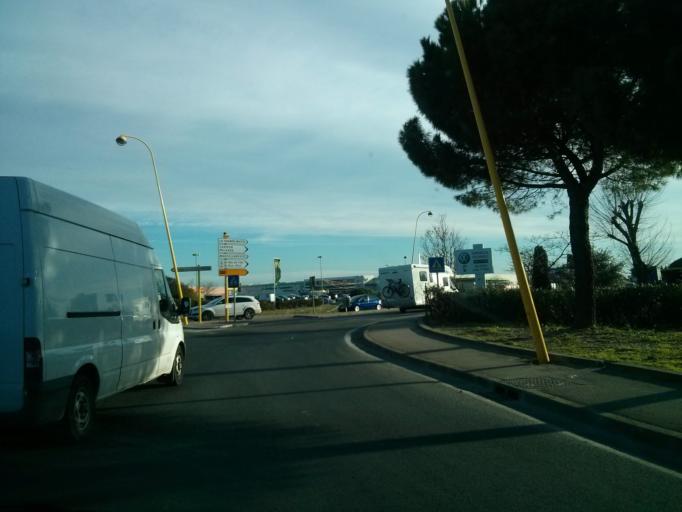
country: FR
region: Languedoc-Roussillon
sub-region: Departement de l'Herault
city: Lunel
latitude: 43.6832
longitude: 4.1501
